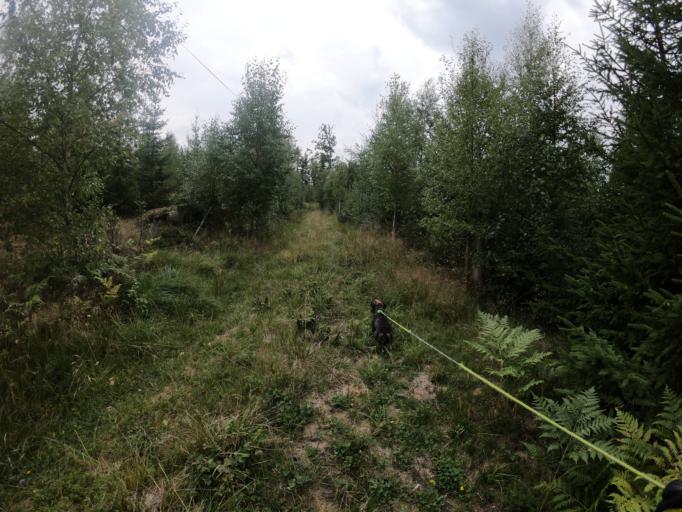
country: SE
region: Joenkoeping
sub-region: Vetlanda Kommun
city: Landsbro
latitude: 57.3153
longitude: 14.8589
